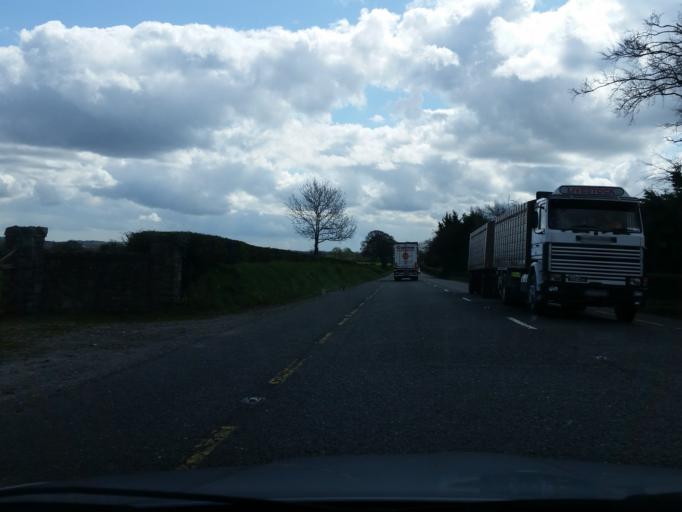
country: IE
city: Kentstown
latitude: 53.6127
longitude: -6.4788
